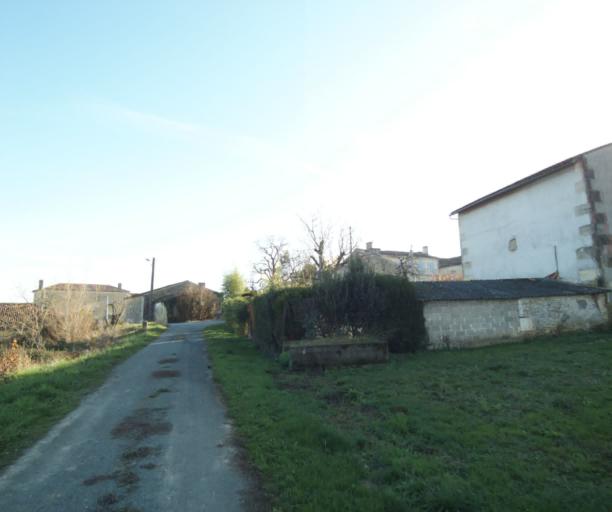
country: FR
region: Poitou-Charentes
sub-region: Departement de la Charente-Maritime
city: Burie
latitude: 45.7780
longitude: -0.4094
